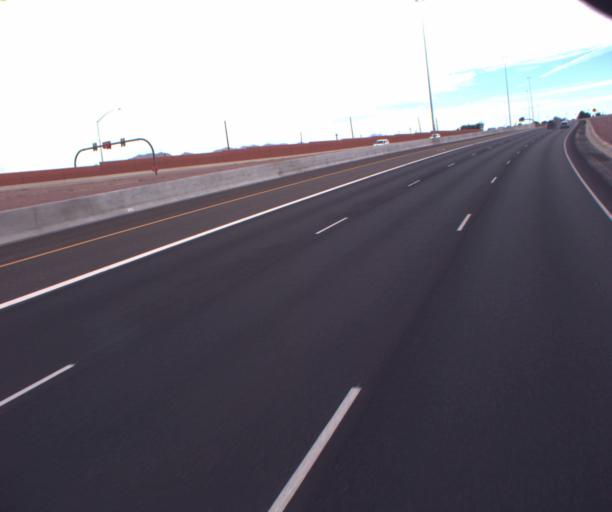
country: US
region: Arizona
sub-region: Maricopa County
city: Mesa
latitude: 33.4821
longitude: -111.7524
